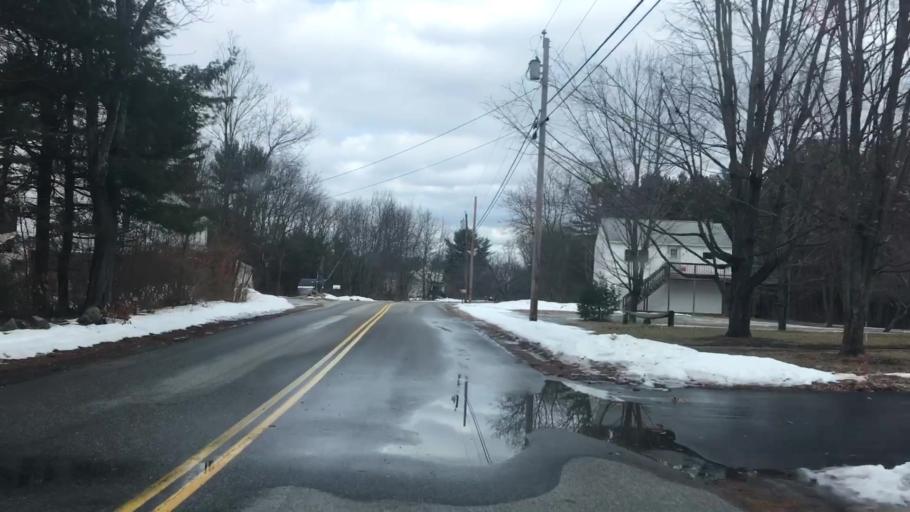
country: US
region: Maine
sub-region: York County
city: Wells Beach Station
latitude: 43.3074
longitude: -70.6553
